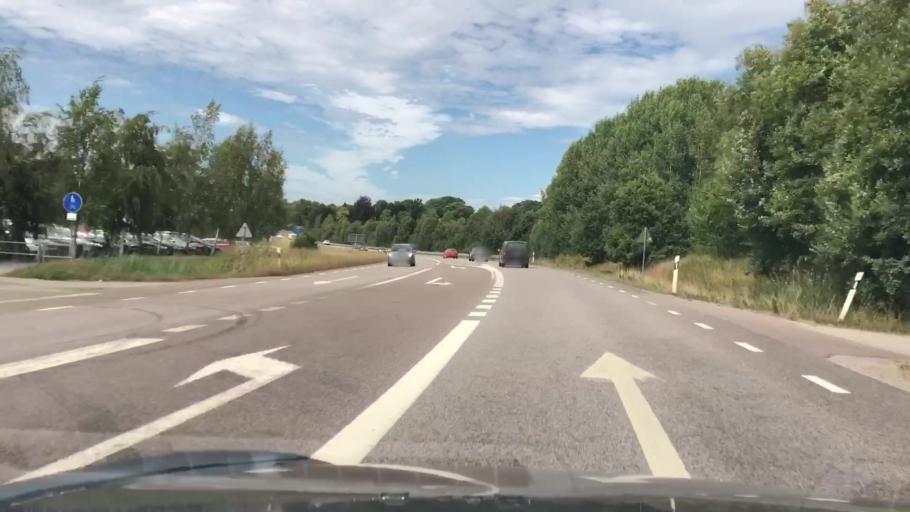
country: SE
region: Blekinge
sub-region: Karlskrona Kommun
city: Rodeby
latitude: 56.1960
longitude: 15.6964
